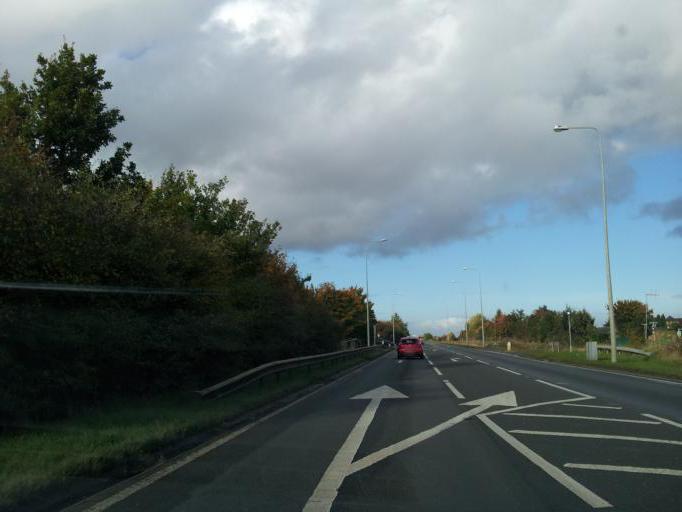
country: GB
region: England
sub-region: Lincolnshire
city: Sutton Bridge
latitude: 52.7666
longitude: 0.1819
